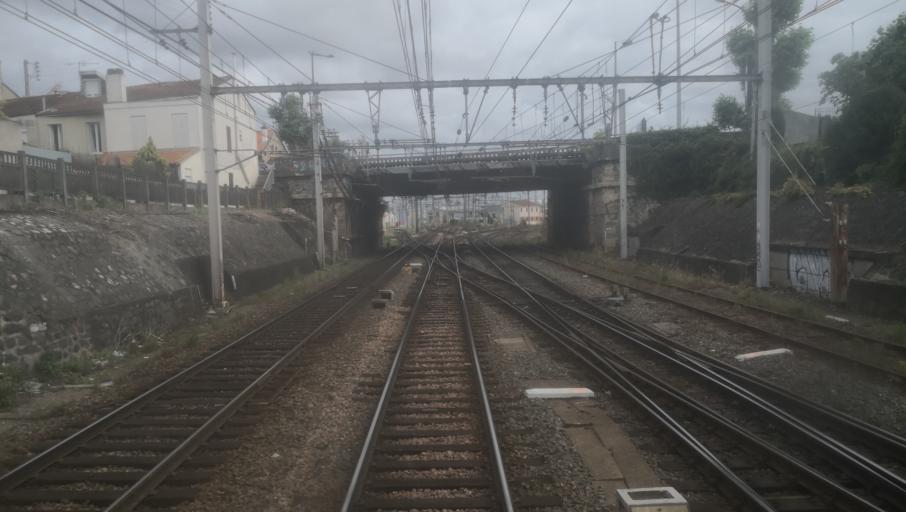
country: FR
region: Aquitaine
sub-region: Departement de la Gironde
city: Begles
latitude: 44.8121
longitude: -0.5597
